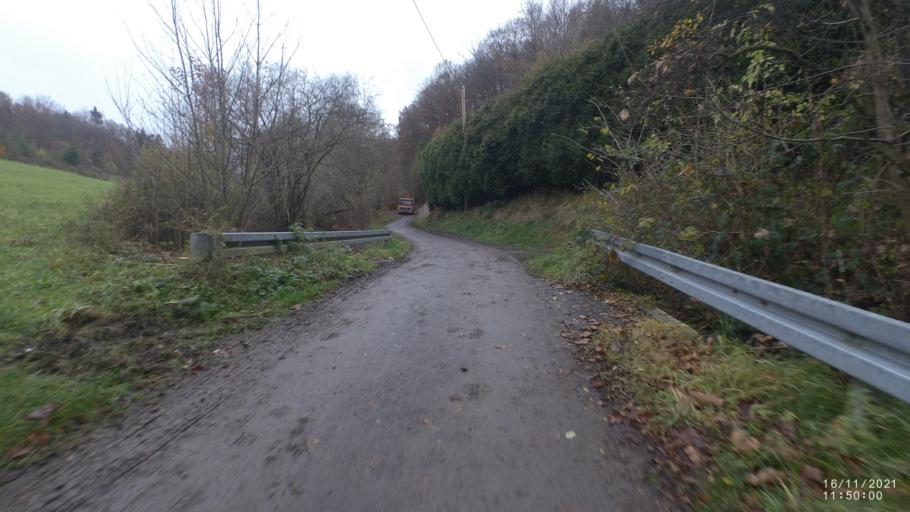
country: DE
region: North Rhine-Westphalia
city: Werdohl
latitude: 51.2462
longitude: 7.8046
